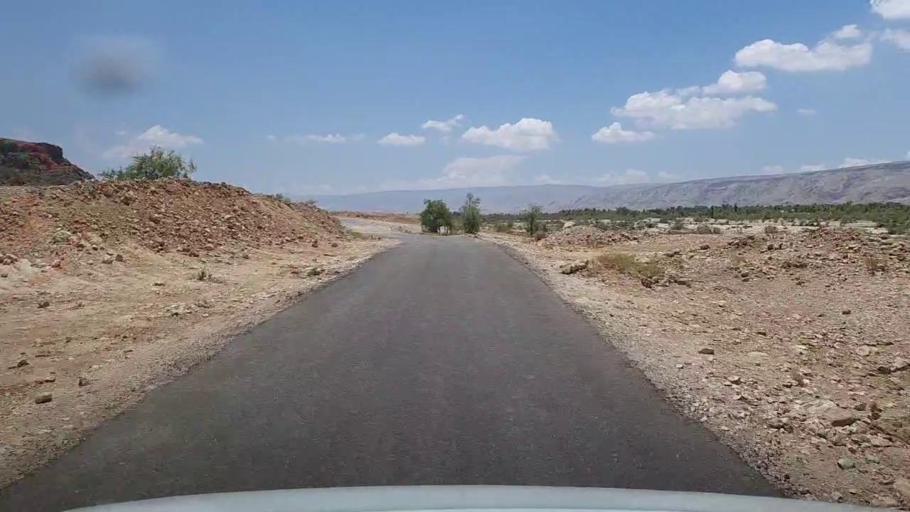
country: PK
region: Sindh
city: Bhan
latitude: 26.2926
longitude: 67.5333
